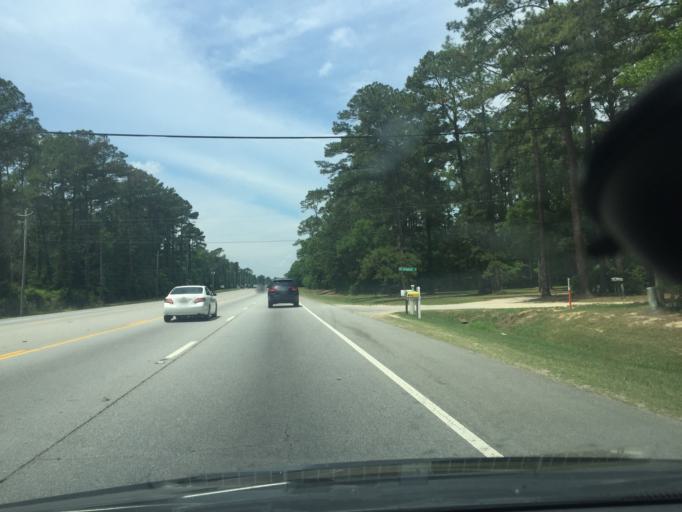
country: US
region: Georgia
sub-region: Chatham County
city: Bloomingdale
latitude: 32.1402
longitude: -81.3231
